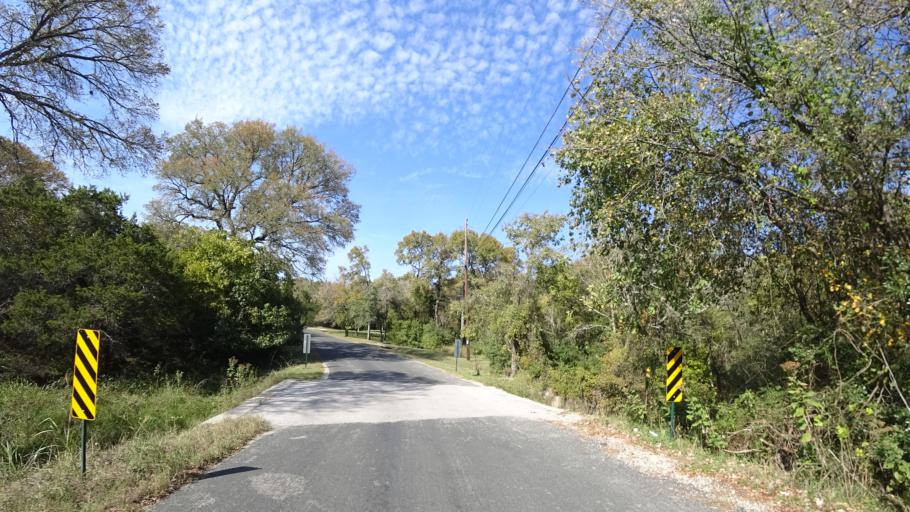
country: US
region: Texas
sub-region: Travis County
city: Barton Creek
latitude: 30.2232
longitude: -97.9241
